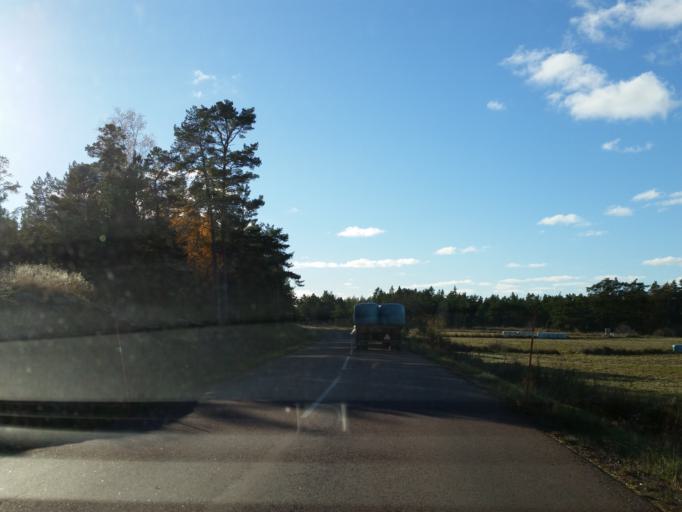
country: AX
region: Alands landsbygd
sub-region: Geta
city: Geta
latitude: 60.3672
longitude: 19.7932
